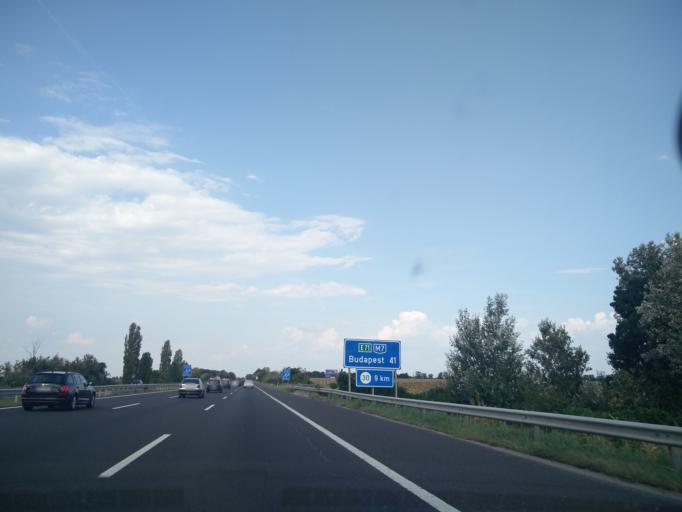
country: HU
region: Fejer
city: Kapolnasnyek
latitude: 47.2636
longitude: 18.6833
